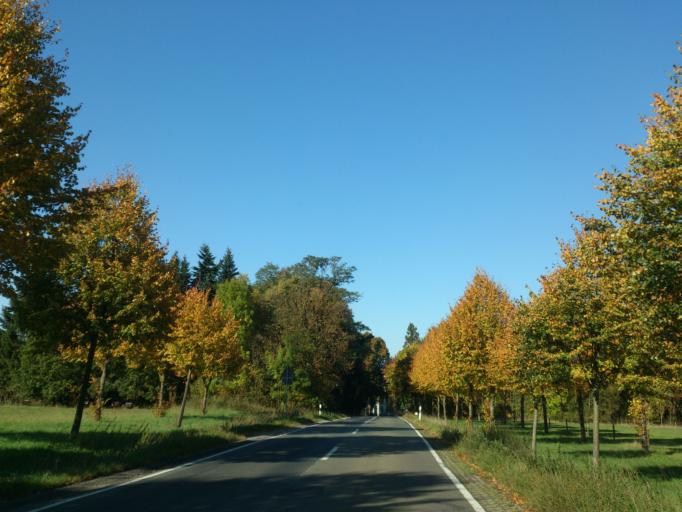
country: DE
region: Hesse
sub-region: Regierungsbezirk Kassel
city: Calden
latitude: 51.3897
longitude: 9.4166
